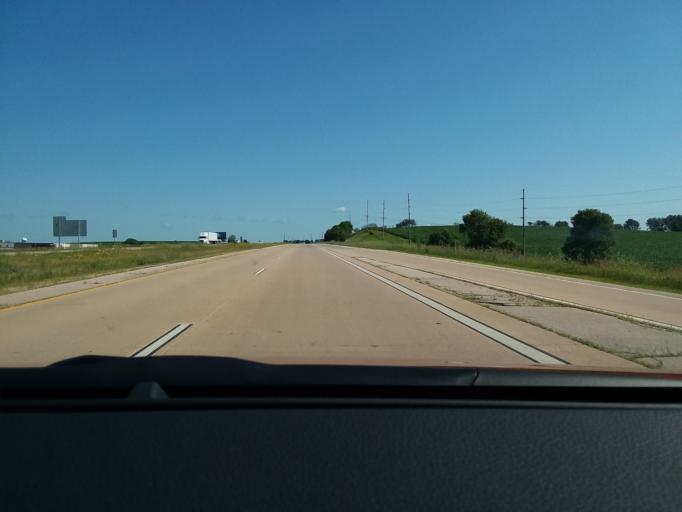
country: US
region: Wisconsin
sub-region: Dane County
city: Windsor
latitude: 43.1980
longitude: -89.3240
